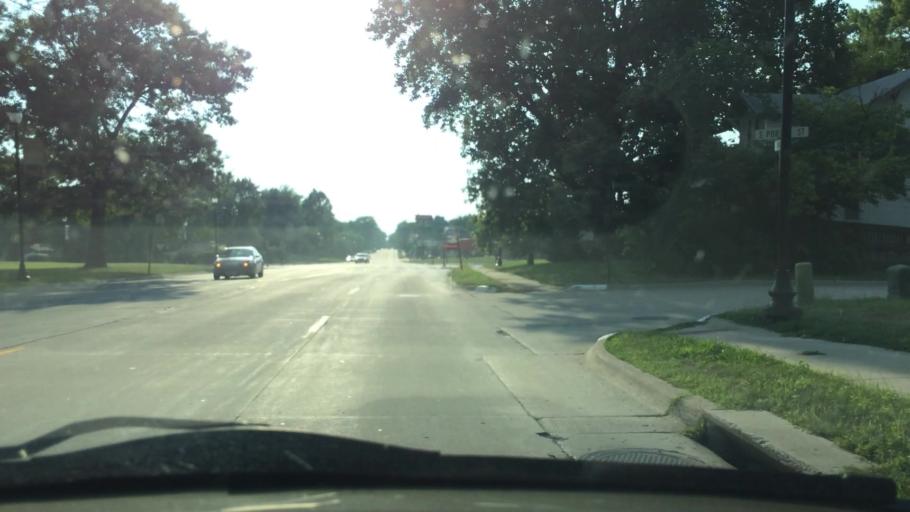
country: US
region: Iowa
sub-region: Henry County
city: Mount Pleasant
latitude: 40.9639
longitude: -91.5380
